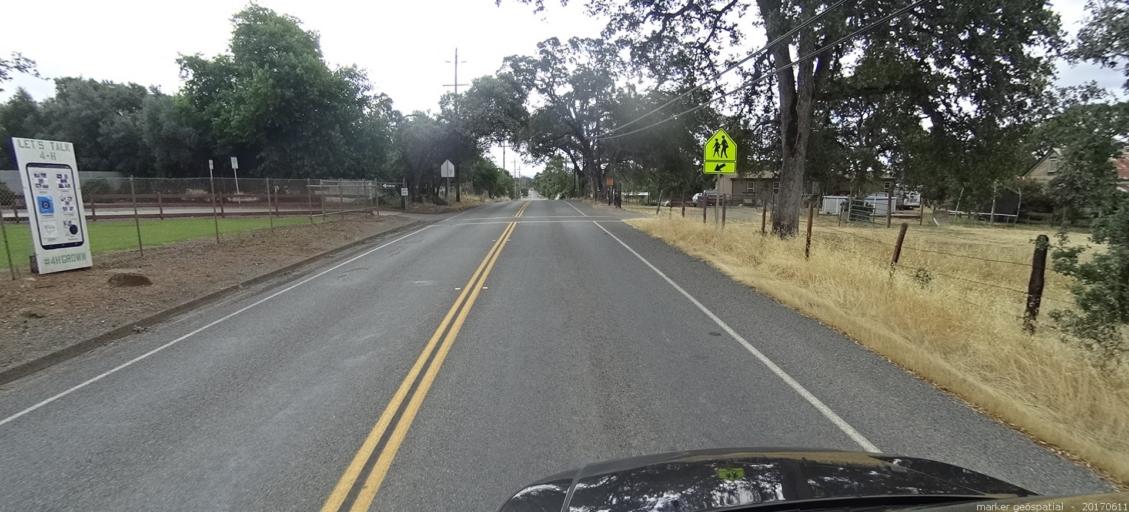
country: US
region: California
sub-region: Yuba County
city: Loma Rica
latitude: 39.3901
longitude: -121.4079
